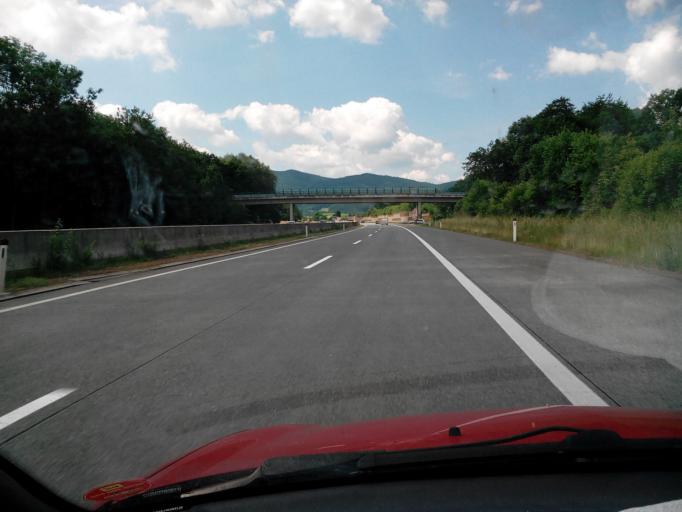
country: AT
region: Upper Austria
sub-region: Politischer Bezirk Vocklabruck
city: Oberwang
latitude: 47.8937
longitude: 13.4390
